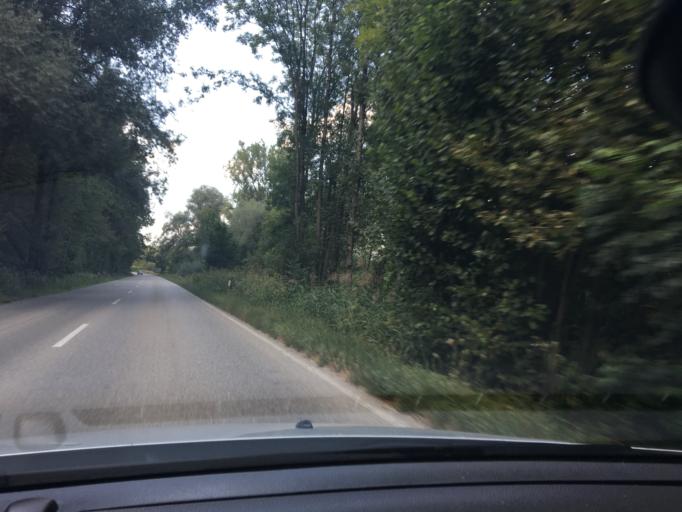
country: DE
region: Bavaria
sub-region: Upper Bavaria
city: Altoetting
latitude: 48.2439
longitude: 12.6649
